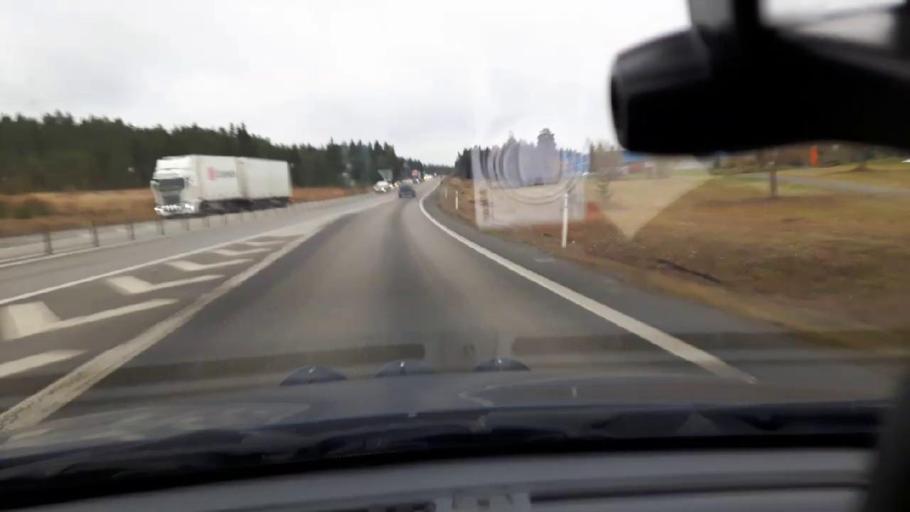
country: SE
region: Jaemtland
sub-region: OEstersunds Kommun
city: Ostersund
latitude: 63.1781
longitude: 14.6926
